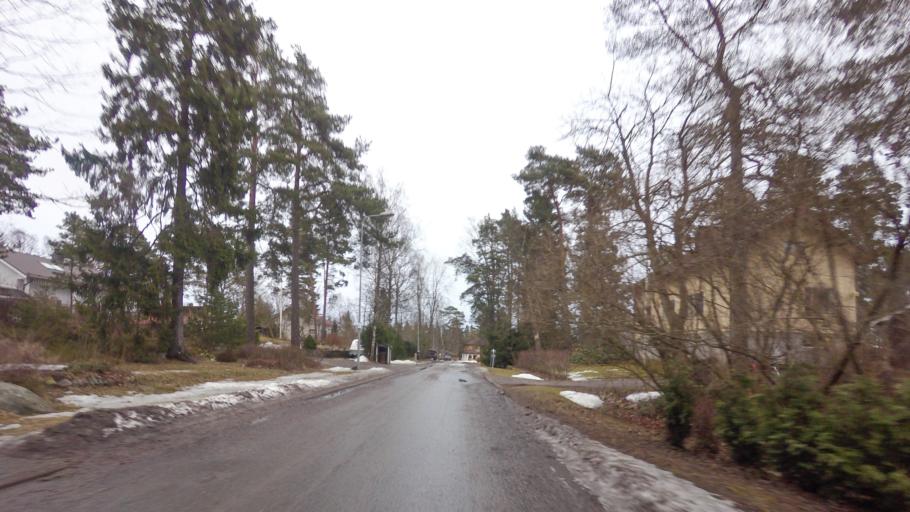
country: FI
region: Uusimaa
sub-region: Helsinki
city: Helsinki
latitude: 60.1640
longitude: 25.0536
